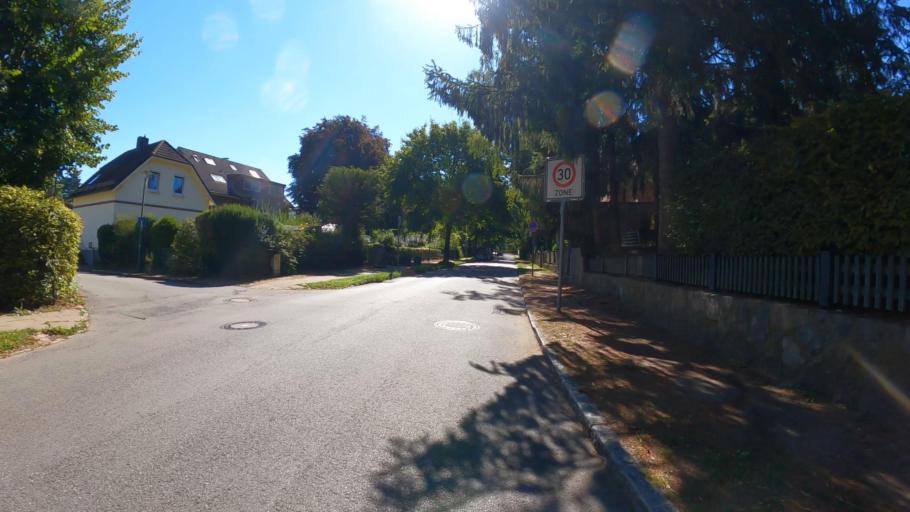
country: DE
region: Schleswig-Holstein
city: Aumuhle
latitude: 53.5263
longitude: 10.3136
